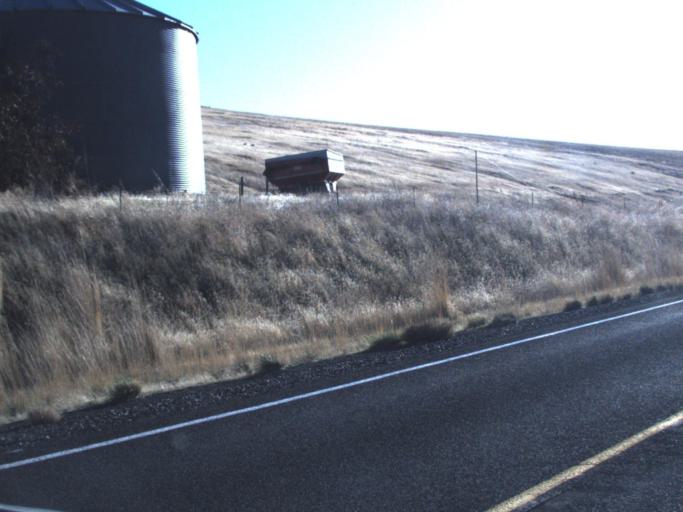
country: US
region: Washington
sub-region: Garfield County
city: Pomeroy
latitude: 46.5125
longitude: -117.7871
